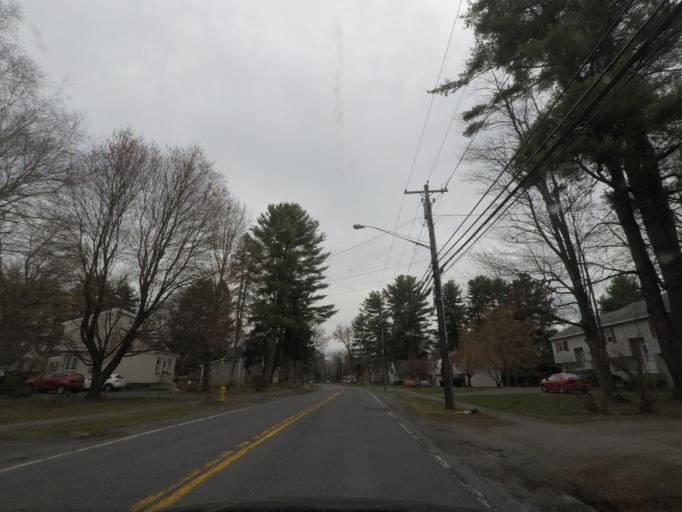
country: US
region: New York
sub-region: Albany County
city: Delmar
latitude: 42.6189
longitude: -73.8201
